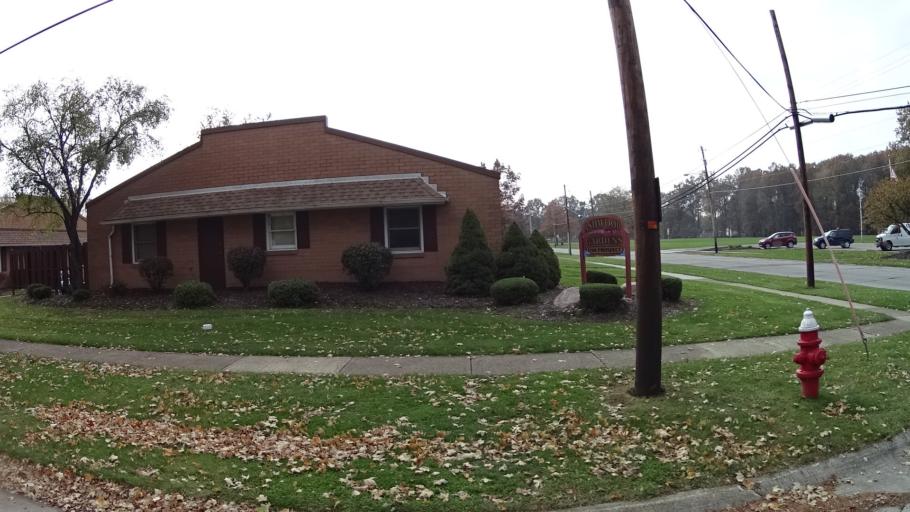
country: US
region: Ohio
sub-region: Lorain County
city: Elyria
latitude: 41.3585
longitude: -82.0885
